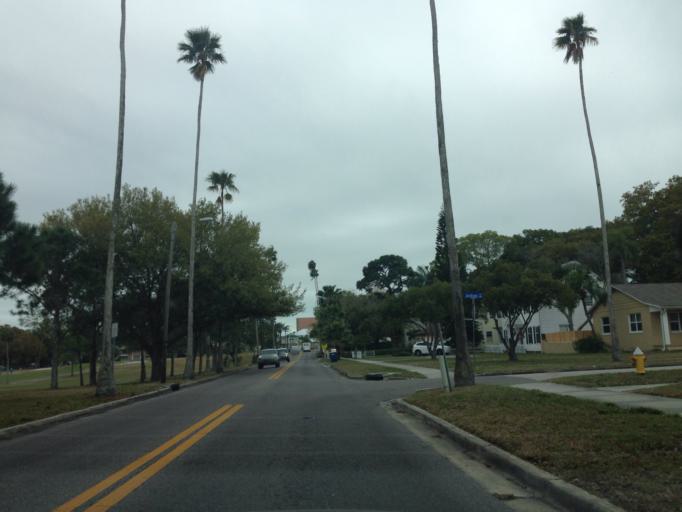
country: US
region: Florida
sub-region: Pinellas County
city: Clearwater
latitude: 27.9704
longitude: -82.7836
